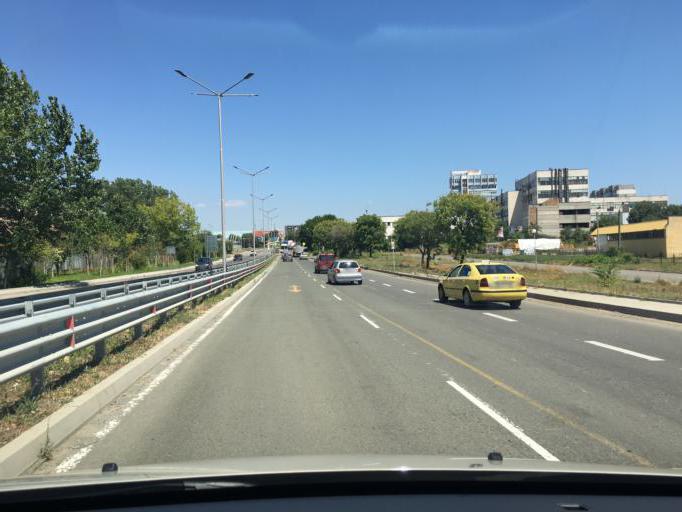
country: BG
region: Burgas
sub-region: Obshtina Burgas
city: Burgas
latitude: 42.5173
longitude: 27.4375
